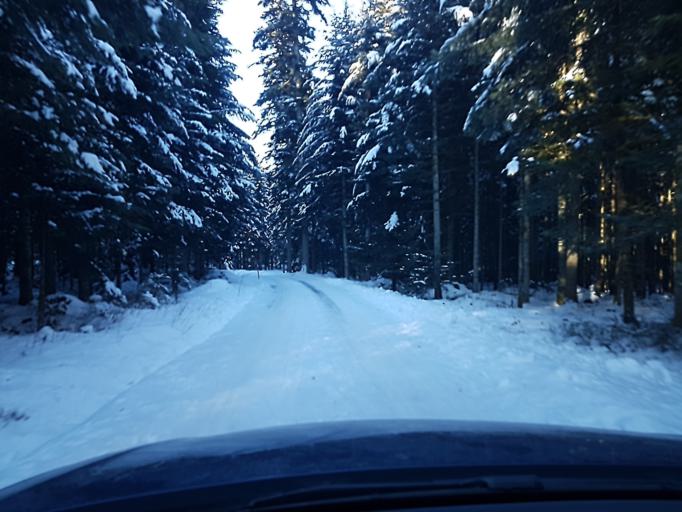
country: DE
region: Baden-Wuerttemberg
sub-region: Freiburg Region
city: Sankt Georgen im Schwarzwald
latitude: 48.1183
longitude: 8.3476
